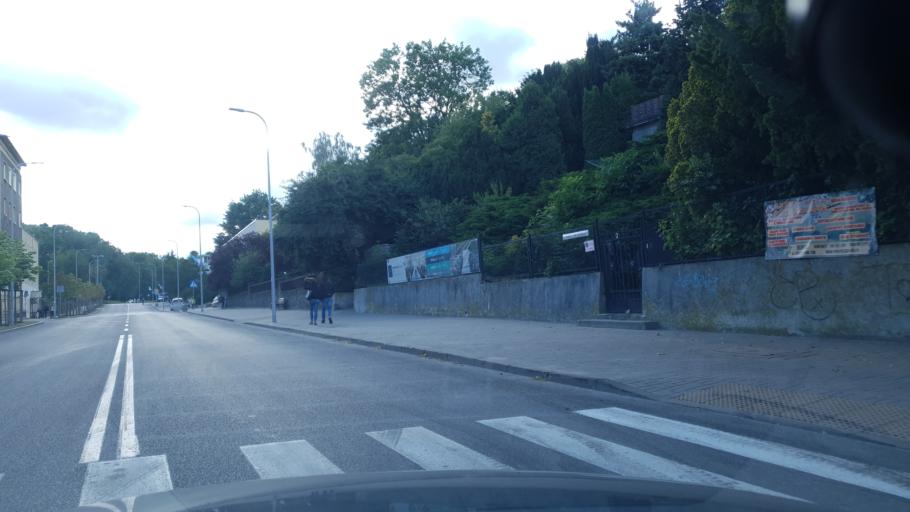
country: PL
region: Pomeranian Voivodeship
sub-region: Gdynia
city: Gdynia
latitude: 54.5080
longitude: 18.5527
